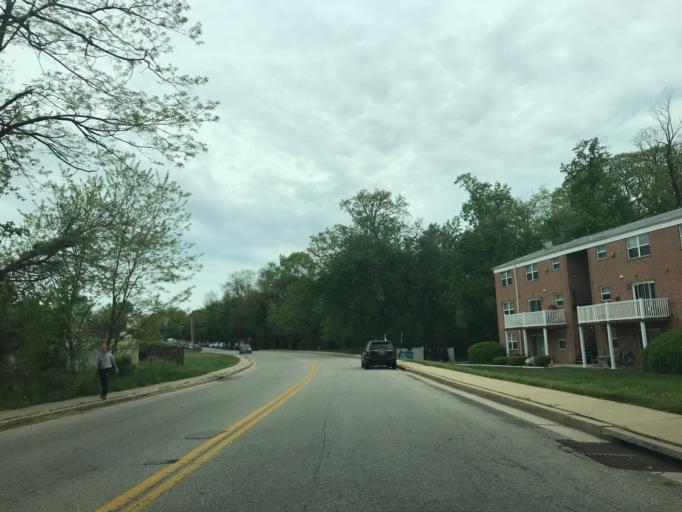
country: US
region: Maryland
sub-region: Baltimore County
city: Catonsville
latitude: 39.2638
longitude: -76.7311
